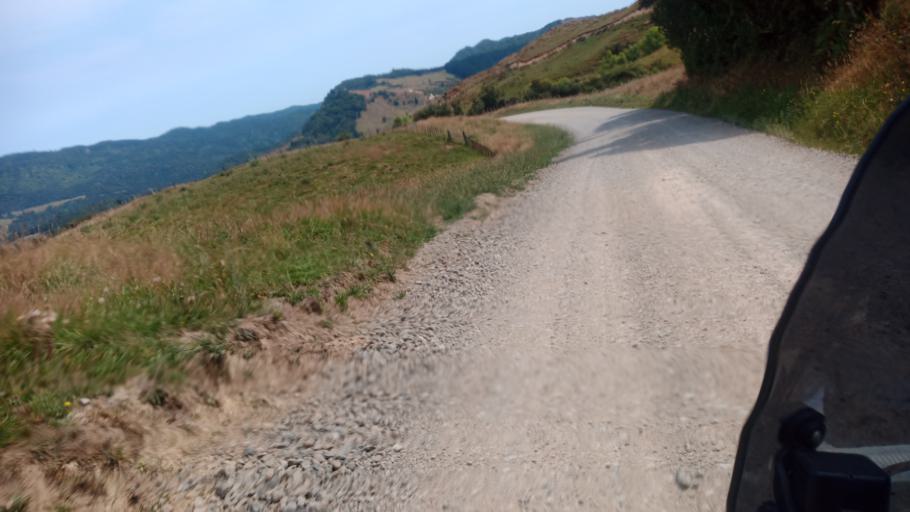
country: NZ
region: Bay of Plenty
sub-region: Opotiki District
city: Opotiki
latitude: -37.6559
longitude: 178.1240
